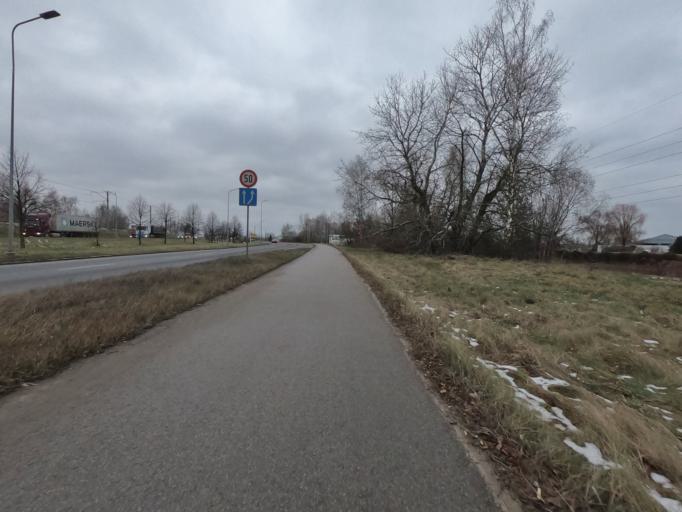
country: LV
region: Riga
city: Jaunciems
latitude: 57.0285
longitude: 24.1391
